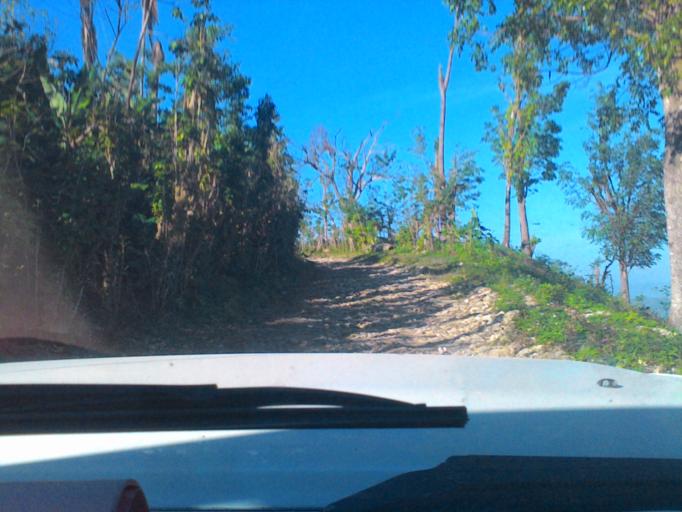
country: HT
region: Grandans
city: Jeremie
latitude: 18.5118
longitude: -74.0896
